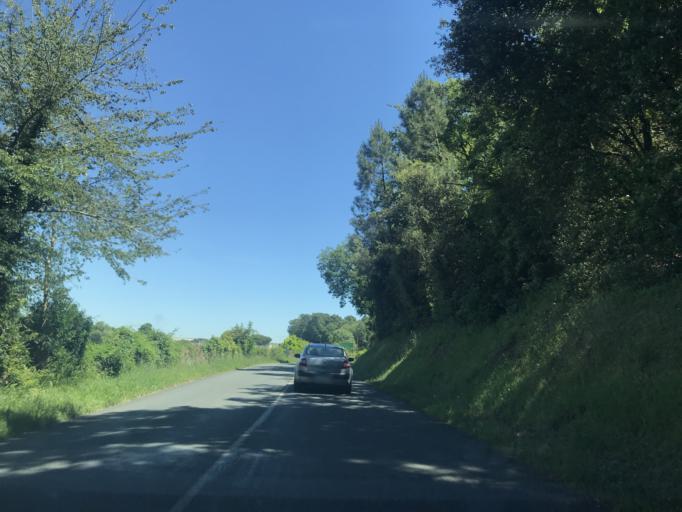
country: FR
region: Poitou-Charentes
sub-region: Departement de la Charente-Maritime
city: Saint-Georges-de-Didonne
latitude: 45.5942
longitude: -0.9733
